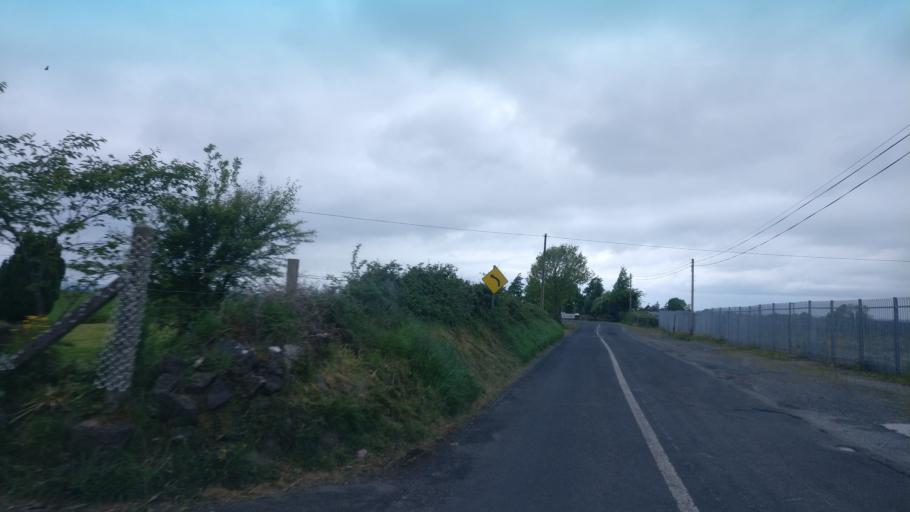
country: IE
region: Connaught
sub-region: County Galway
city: Portumna
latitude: 53.1125
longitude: -8.2771
